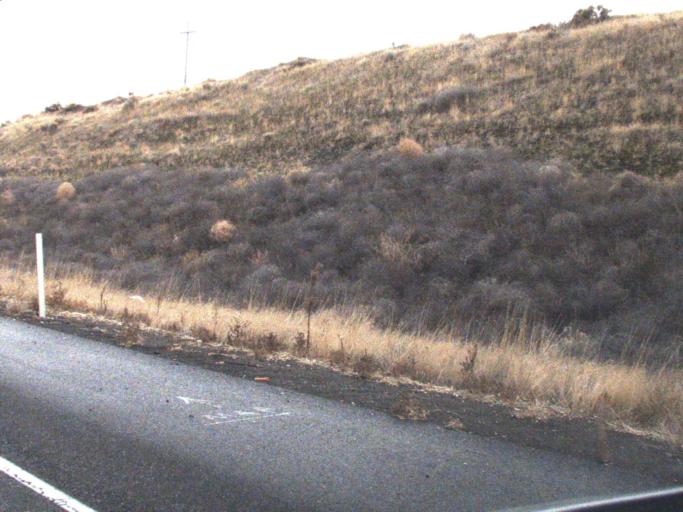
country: US
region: Washington
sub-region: Walla Walla County
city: Burbank
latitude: 46.1697
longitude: -118.9560
